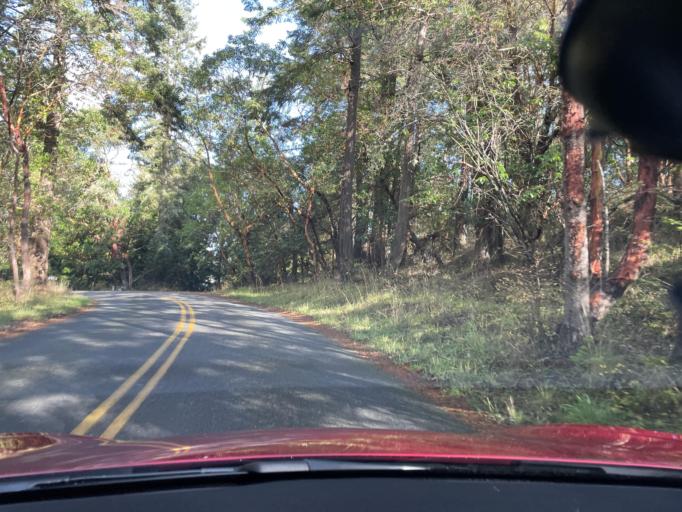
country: US
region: Washington
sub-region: San Juan County
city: Friday Harbor
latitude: 48.5051
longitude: -123.0187
